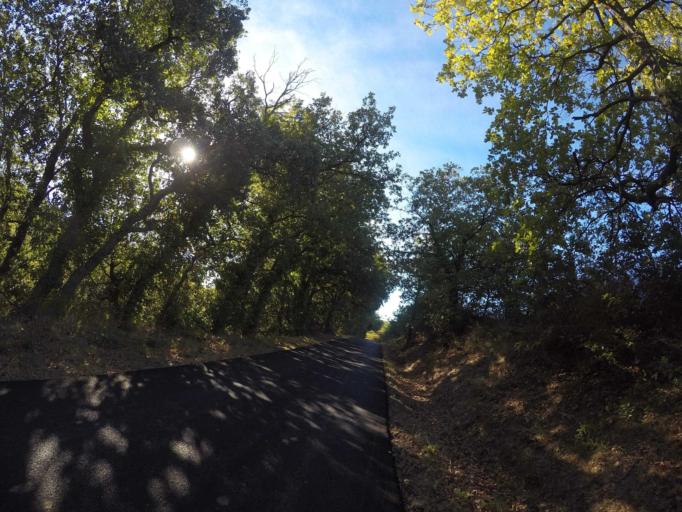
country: FR
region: Languedoc-Roussillon
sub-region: Departement des Pyrenees-Orientales
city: Trouillas
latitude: 42.5724
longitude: 2.7908
